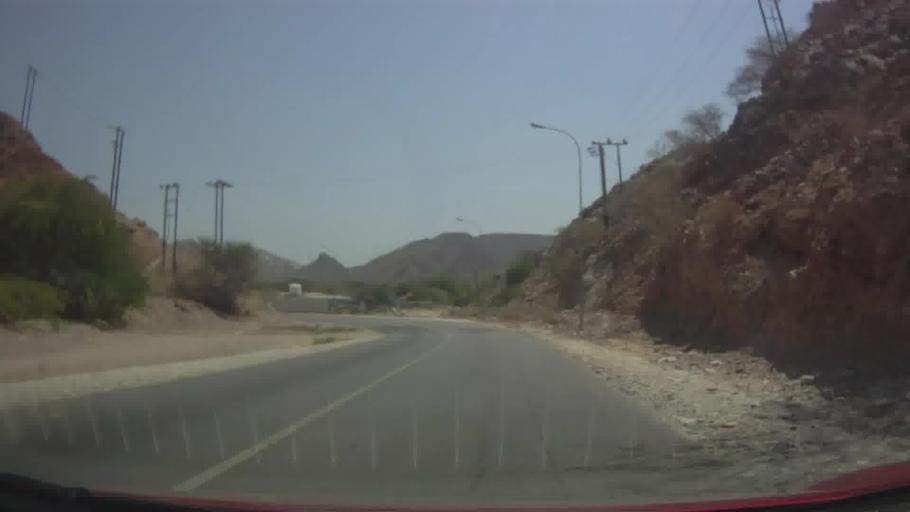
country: OM
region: Muhafazat Masqat
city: Muscat
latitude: 23.5073
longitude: 58.6513
